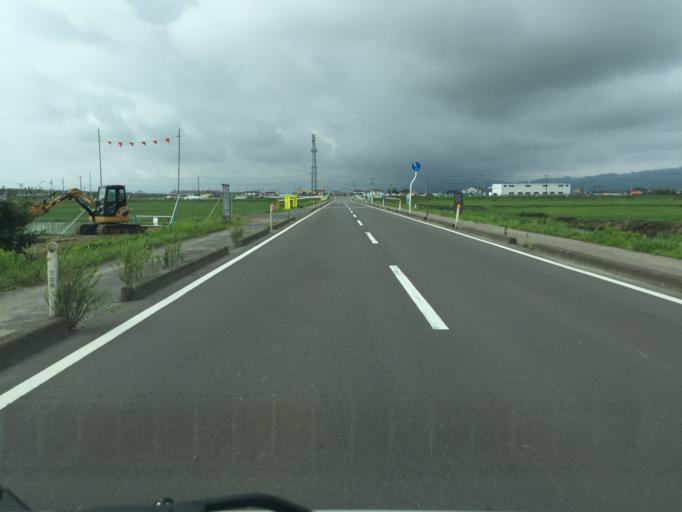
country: JP
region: Miyagi
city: Watari
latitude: 38.0369
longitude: 140.8895
